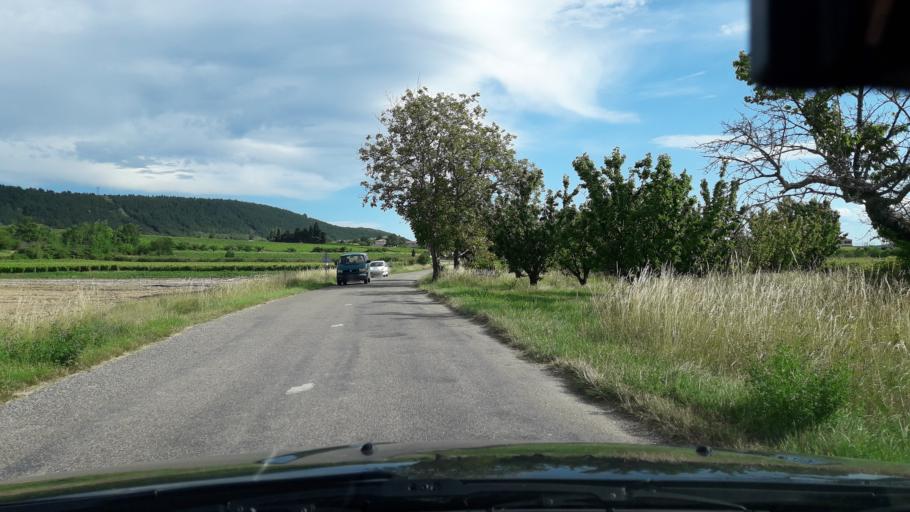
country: FR
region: Rhone-Alpes
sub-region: Departement de l'Ardeche
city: Vesseaux
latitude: 44.6172
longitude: 4.4745
